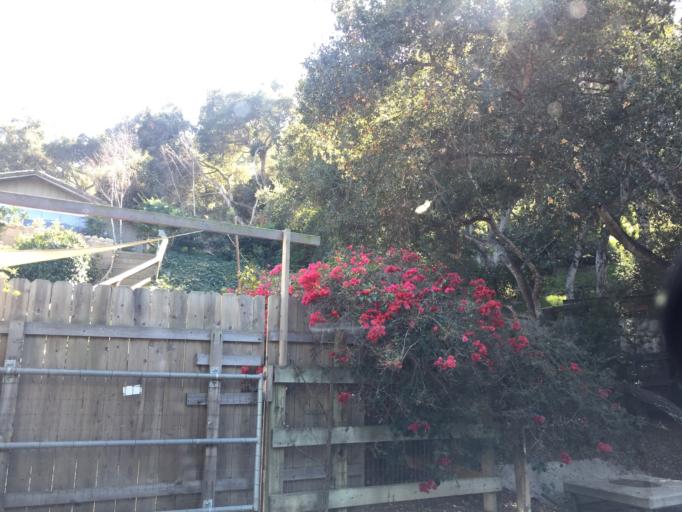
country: US
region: California
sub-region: Santa Barbara County
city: Goleta
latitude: 34.4317
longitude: -119.7806
